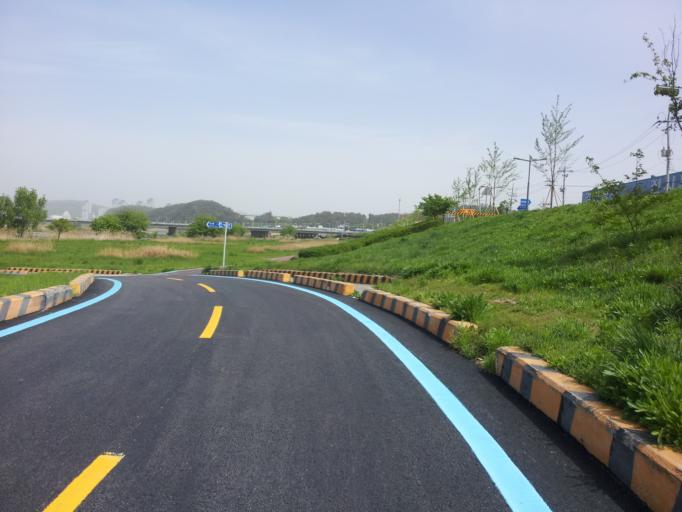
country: KR
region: Daejeon
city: Daejeon
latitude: 36.3528
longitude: 127.4050
